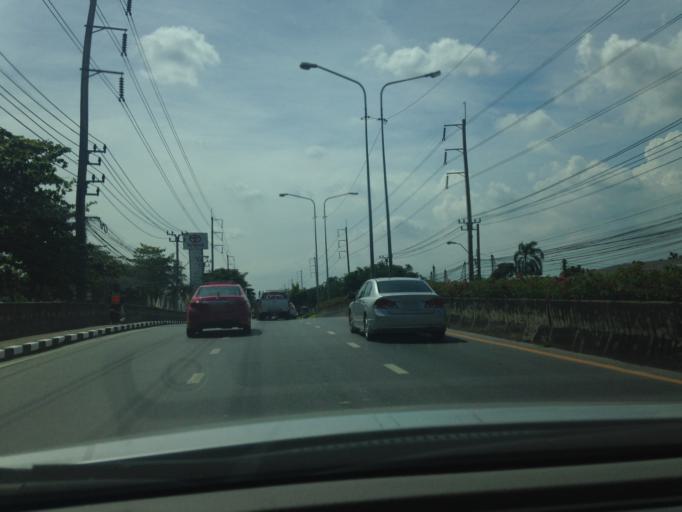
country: TH
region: Bangkok
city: Lat Krabang
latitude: 13.7222
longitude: 100.7301
